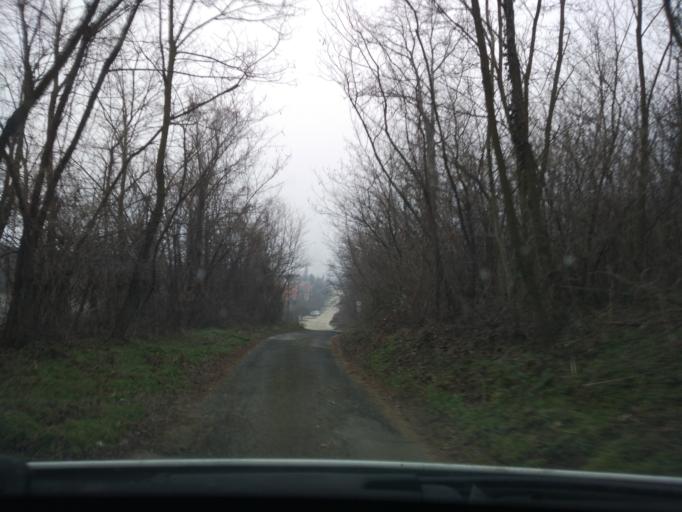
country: HU
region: Veszprem
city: Badacsonytomaj
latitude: 46.8116
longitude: 17.5024
